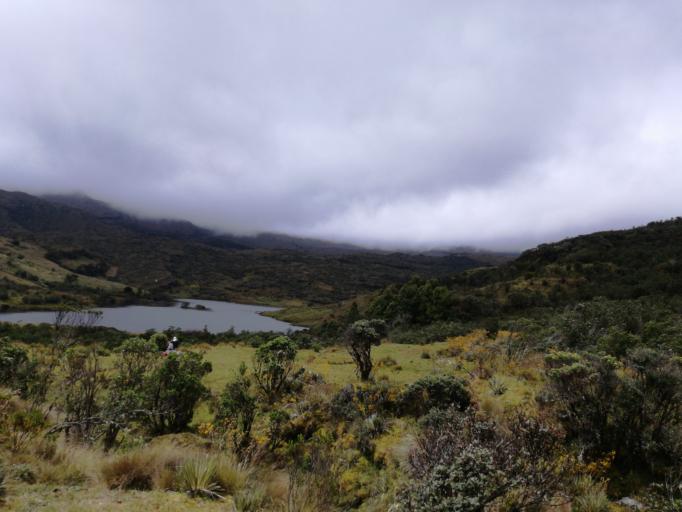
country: CO
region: Boyaca
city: Socha Viejo
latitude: 5.8949
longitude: -72.6772
